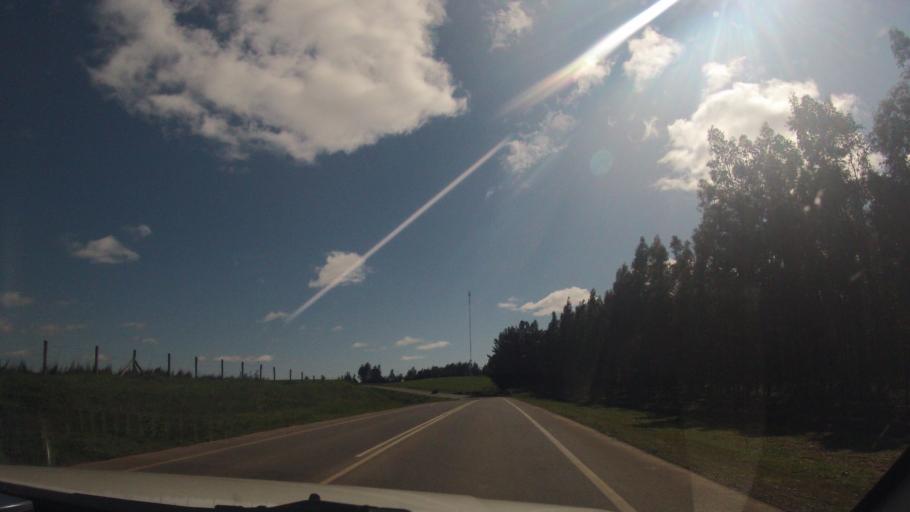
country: CL
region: Araucania
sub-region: Provincia de Malleco
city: Traiguen
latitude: -38.2020
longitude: -72.7536
